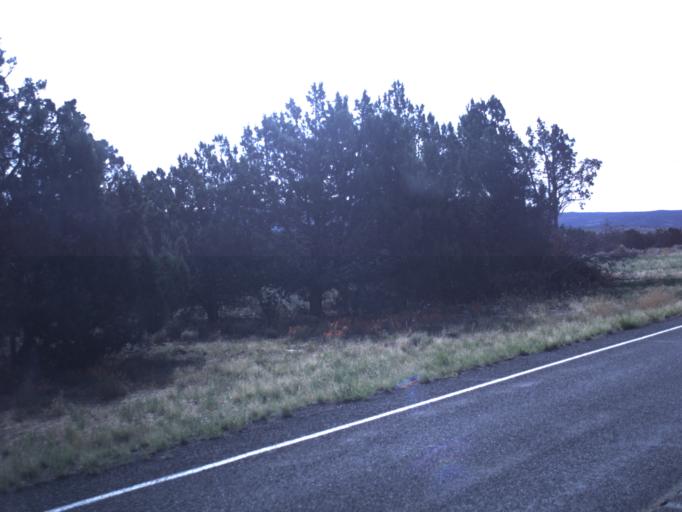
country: US
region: Utah
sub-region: Kane County
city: Kanab
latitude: 37.2537
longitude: -112.7631
